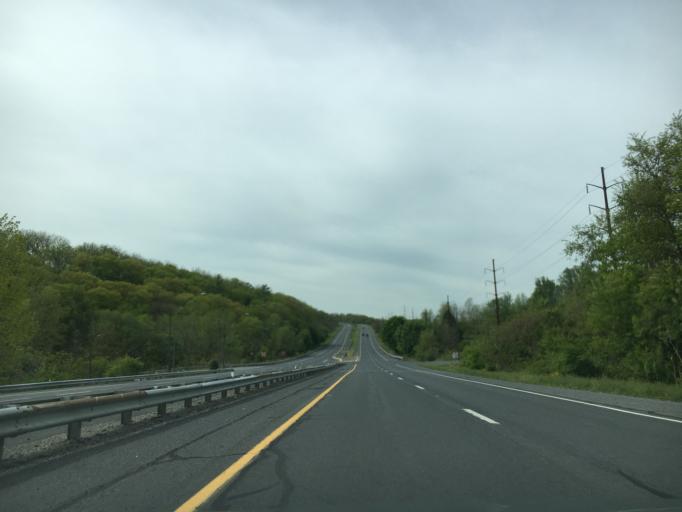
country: US
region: Pennsylvania
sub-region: Lehigh County
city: Cementon
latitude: 40.6985
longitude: -75.5223
